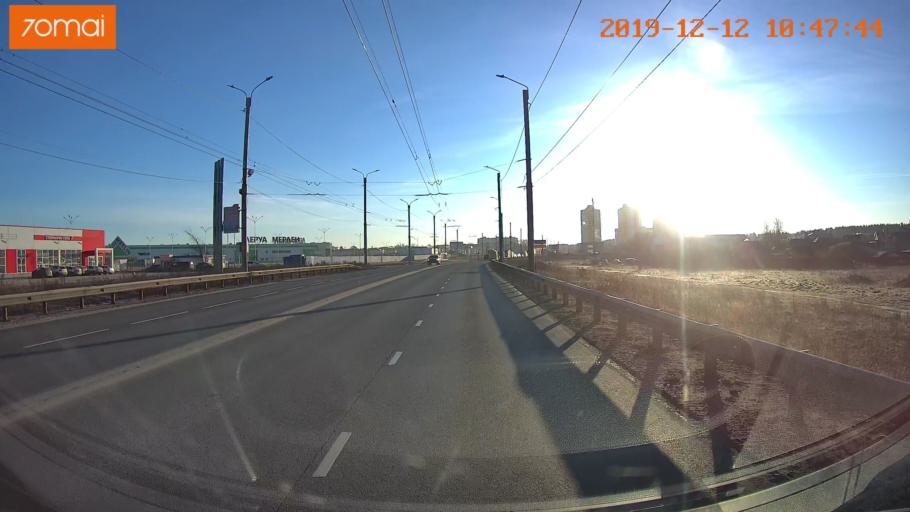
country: RU
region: Ivanovo
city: Kokhma
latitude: 56.9474
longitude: 41.0537
